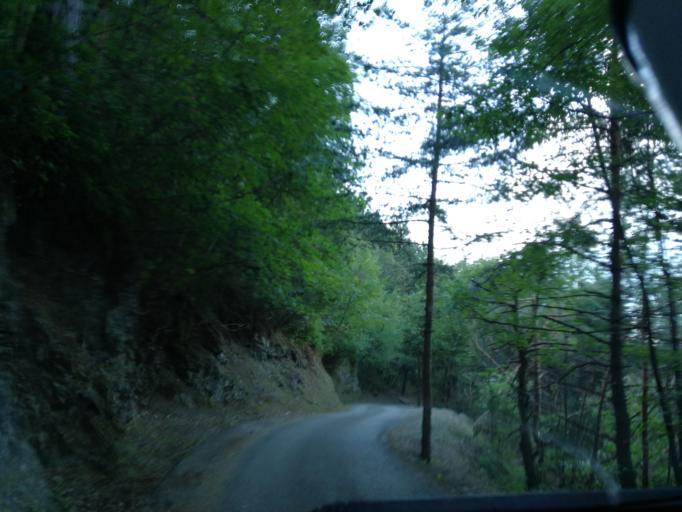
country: IT
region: Trentino-Alto Adige
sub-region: Provincia di Trento
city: Bondone
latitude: 45.8276
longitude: 10.5620
